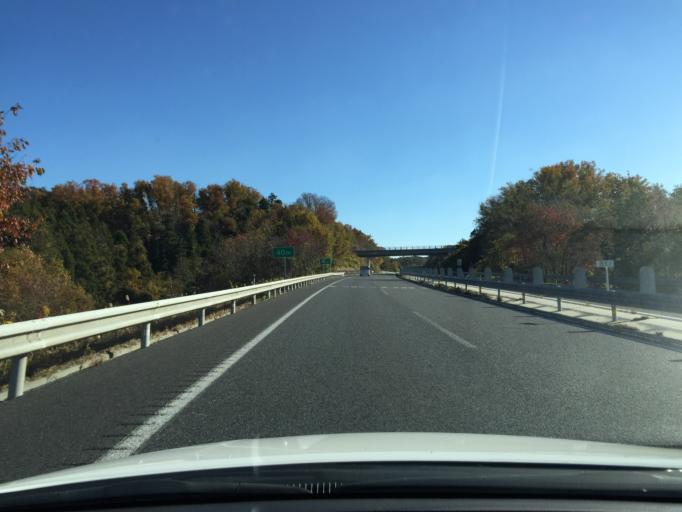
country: JP
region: Fukushima
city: Funehikimachi-funehiki
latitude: 37.4202
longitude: 140.5597
